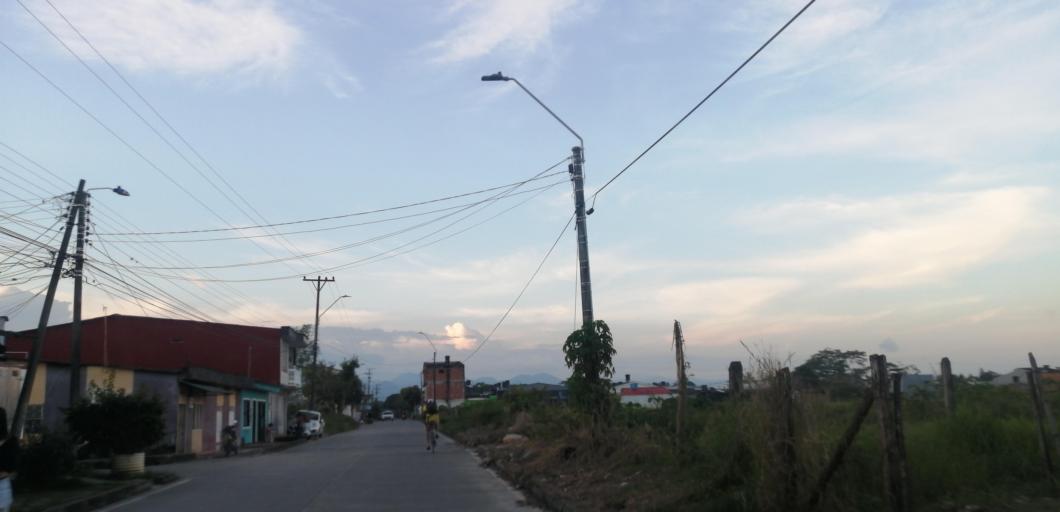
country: CO
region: Meta
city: Acacias
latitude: 3.9933
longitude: -73.7567
